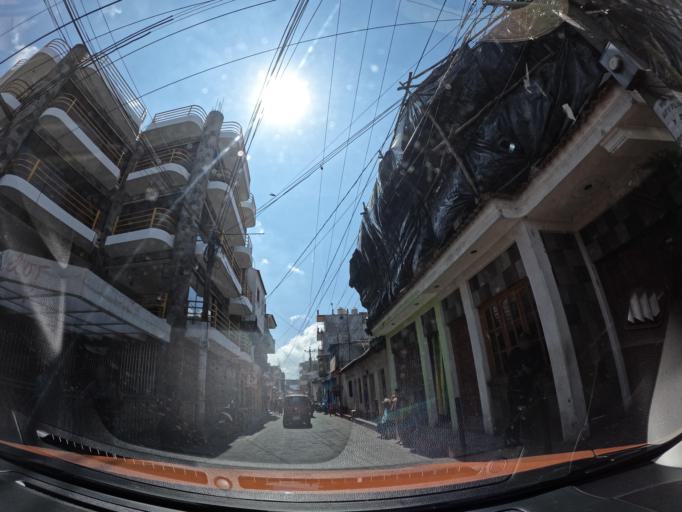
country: GT
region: Solola
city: Santiago Atitlan
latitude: 14.6395
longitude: -91.2311
